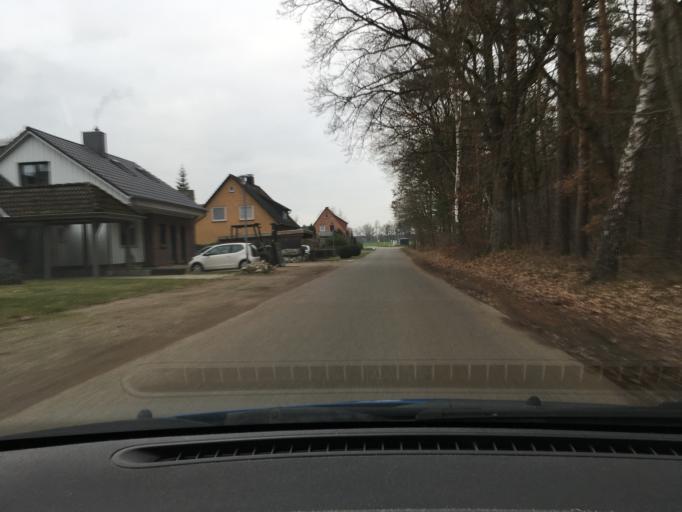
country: DE
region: Lower Saxony
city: Soltau
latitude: 52.9713
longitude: 9.8073
